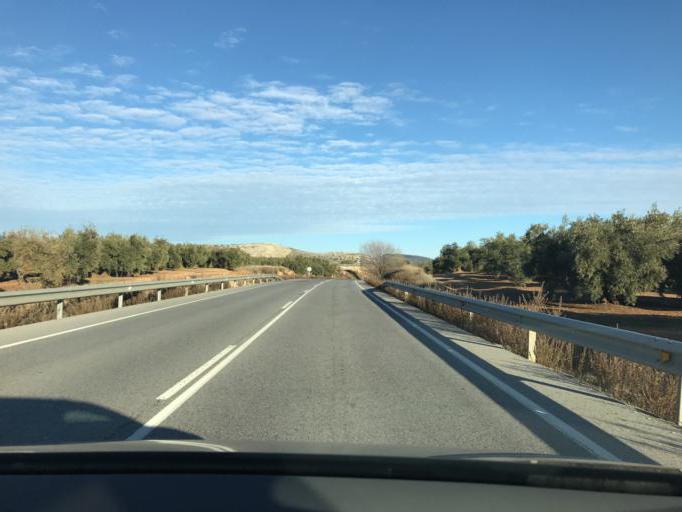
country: ES
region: Andalusia
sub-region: Provincia de Granada
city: Iznalloz
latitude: 37.4021
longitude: -3.5379
